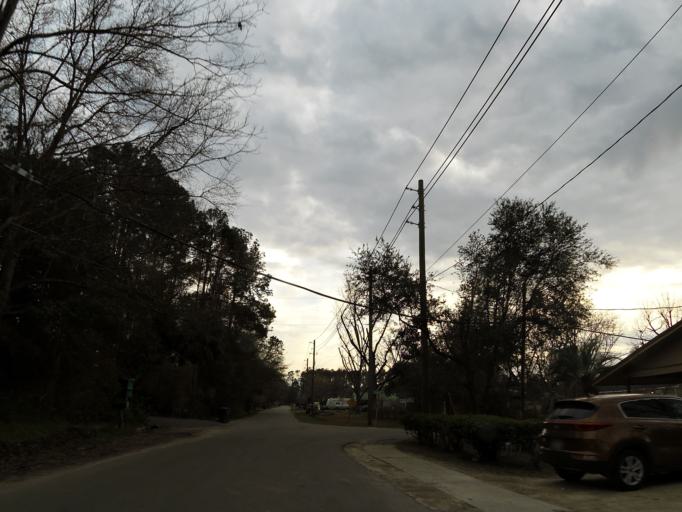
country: US
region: Florida
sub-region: Duval County
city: Baldwin
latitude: 30.2995
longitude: -81.9788
